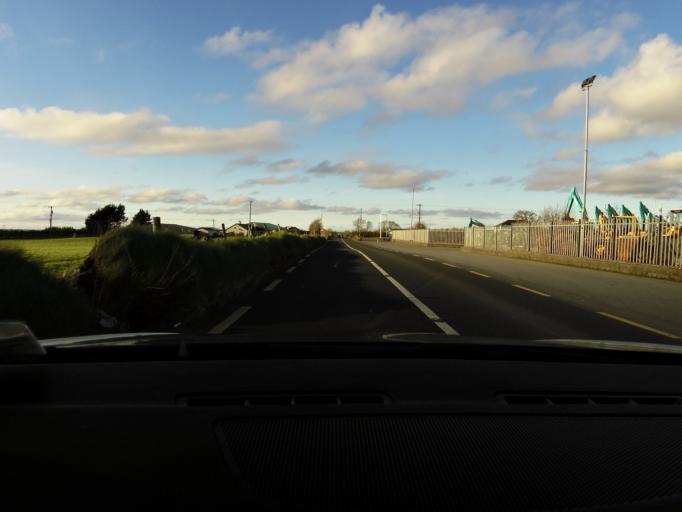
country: IE
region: Connaught
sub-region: Roscommon
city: Roscommon
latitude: 53.6855
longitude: -8.1964
